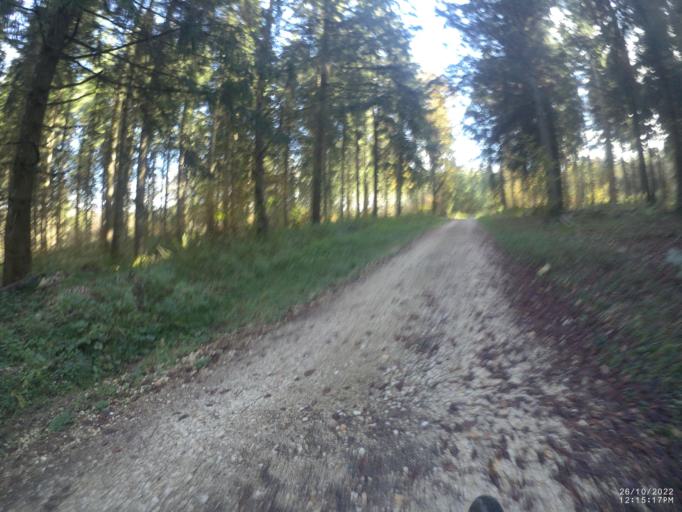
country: DE
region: Baden-Wuerttemberg
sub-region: Regierungsbezirk Stuttgart
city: Wiesensteig
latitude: 48.5463
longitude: 9.6033
